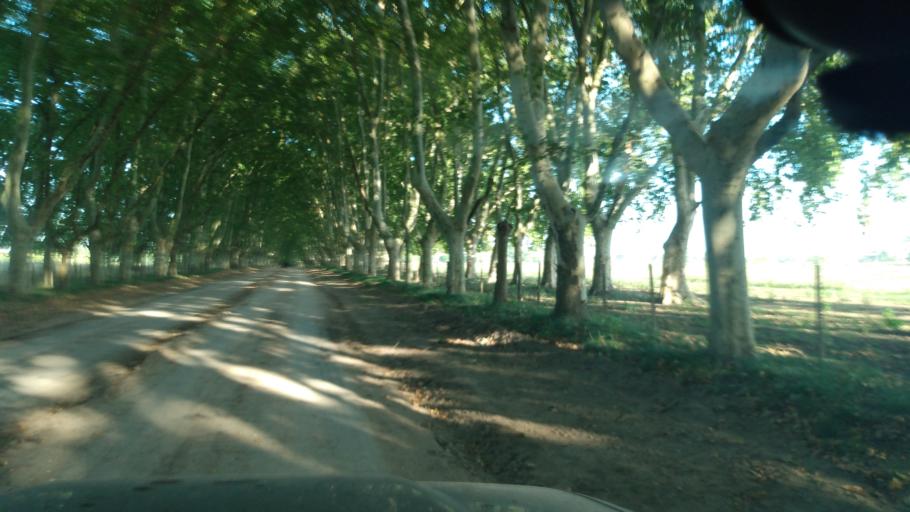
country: AR
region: Buenos Aires
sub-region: Partido de Lujan
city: Lujan
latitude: -34.5823
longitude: -59.0795
